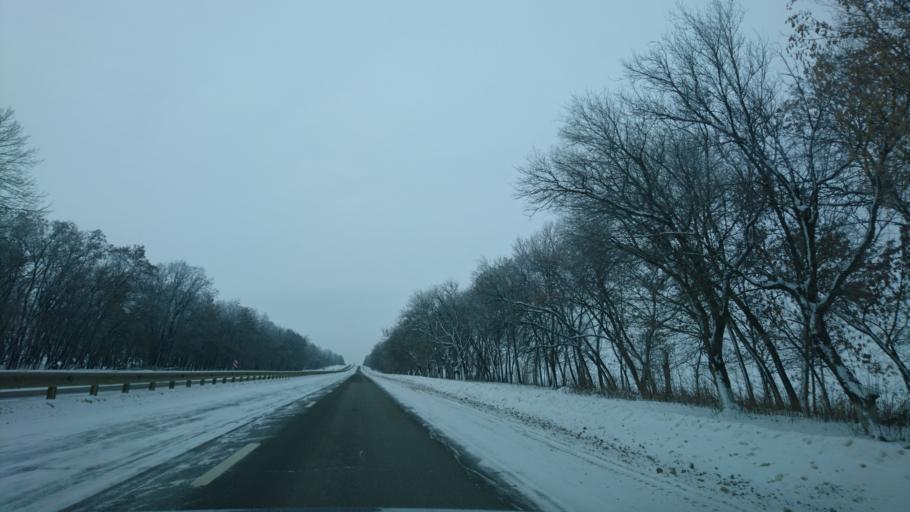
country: RU
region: Belgorod
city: Mayskiy
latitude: 50.4267
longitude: 36.3824
